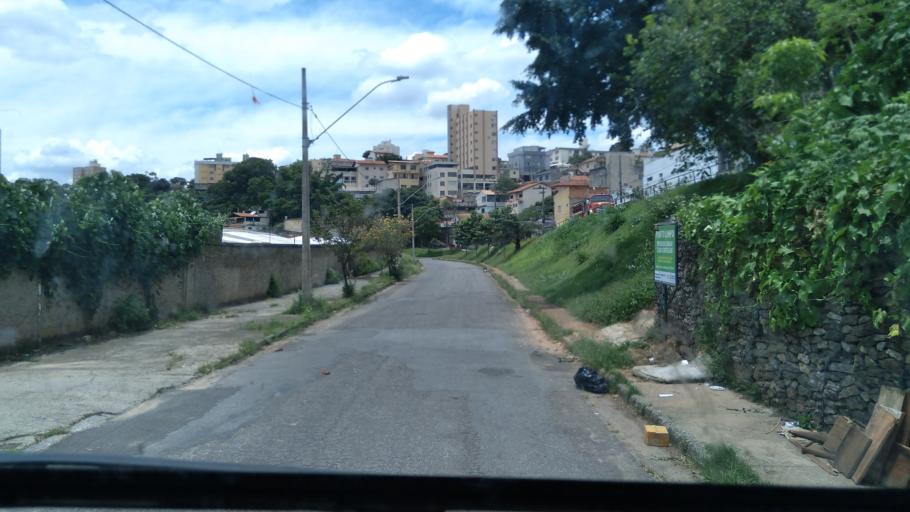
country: BR
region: Minas Gerais
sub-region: Belo Horizonte
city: Belo Horizonte
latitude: -19.9183
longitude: -43.9180
